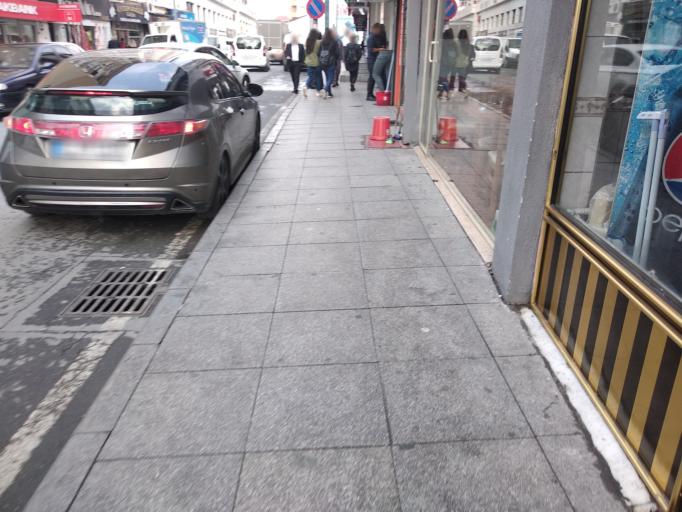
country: TR
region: Istanbul
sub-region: Atasehir
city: Atasehir
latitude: 40.9794
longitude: 29.1131
